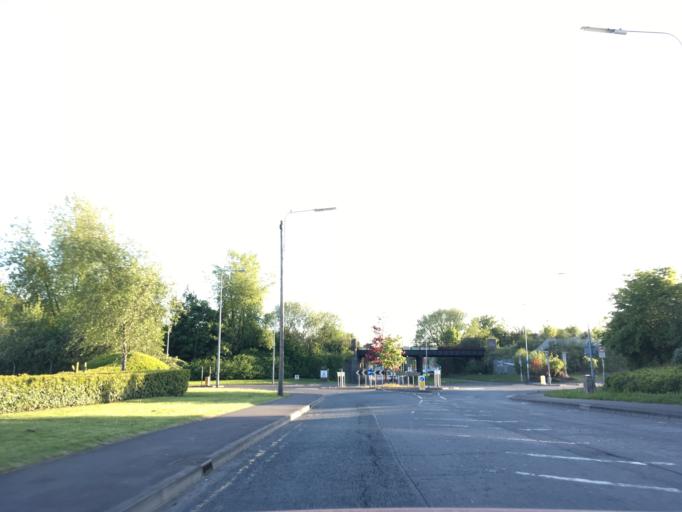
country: GB
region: Wales
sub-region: Newport
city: Newport
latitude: 51.5718
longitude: -2.9956
